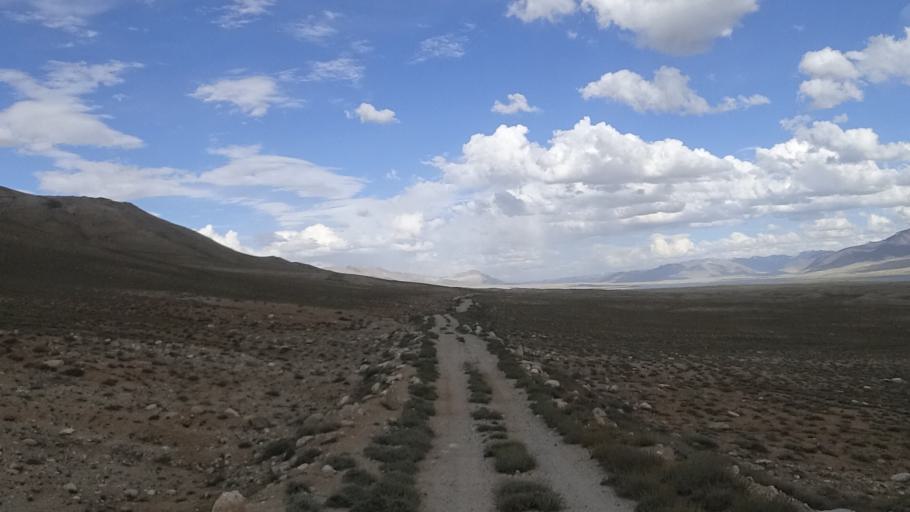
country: TJ
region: Gorno-Badakhshan
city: Murghob
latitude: 37.4680
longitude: 73.5711
